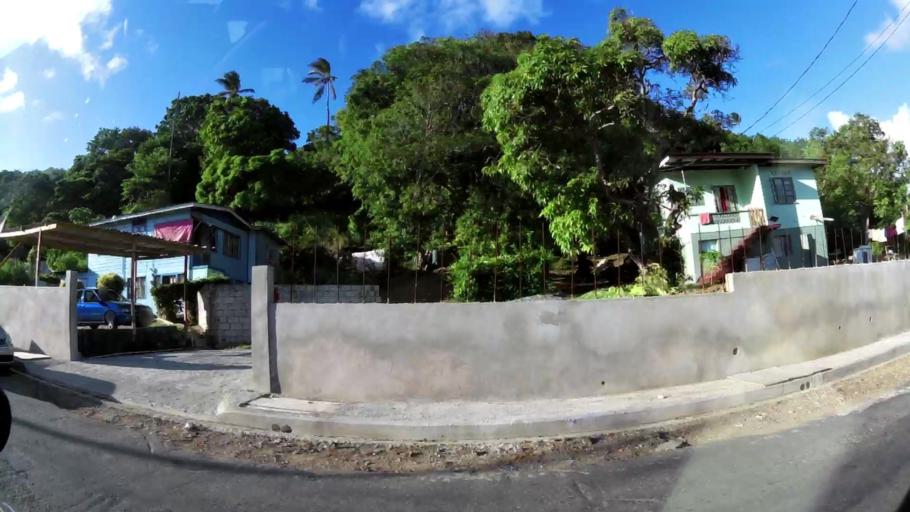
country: TT
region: Tobago
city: Scarborough
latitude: 11.1826
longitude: -60.7011
